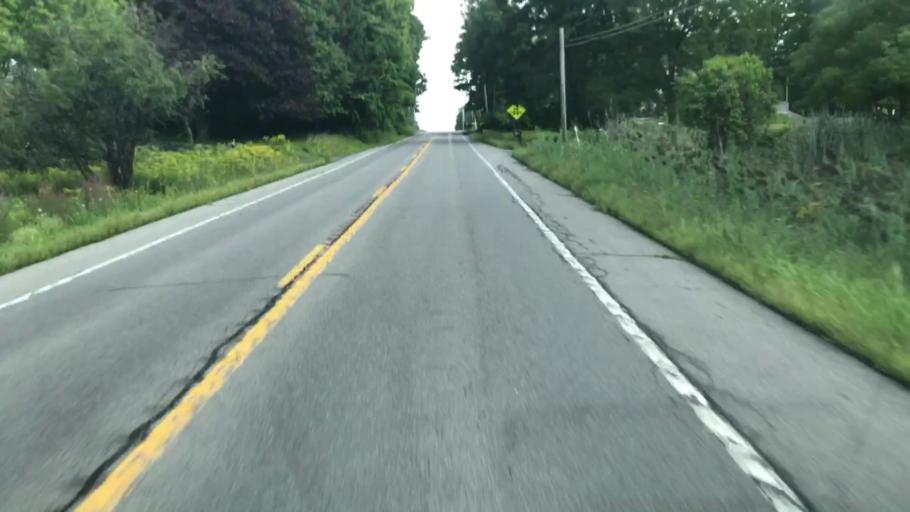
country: US
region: New York
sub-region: Onondaga County
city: Marcellus
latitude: 42.9840
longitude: -76.2901
